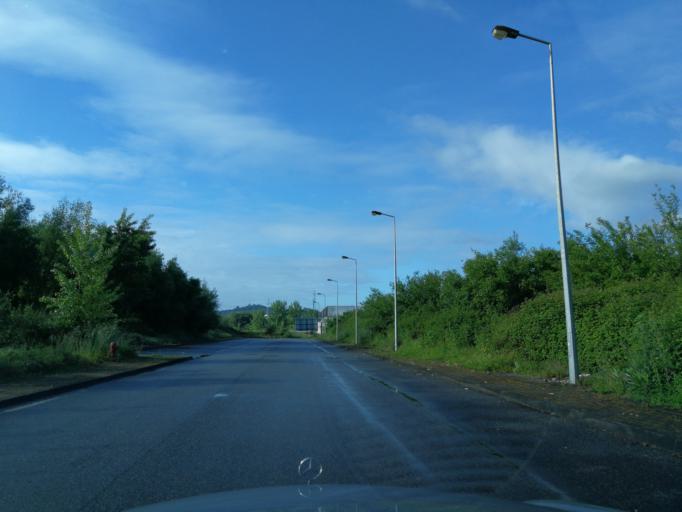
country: PT
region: Braga
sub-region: Braga
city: Braga
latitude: 41.5675
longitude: -8.4477
